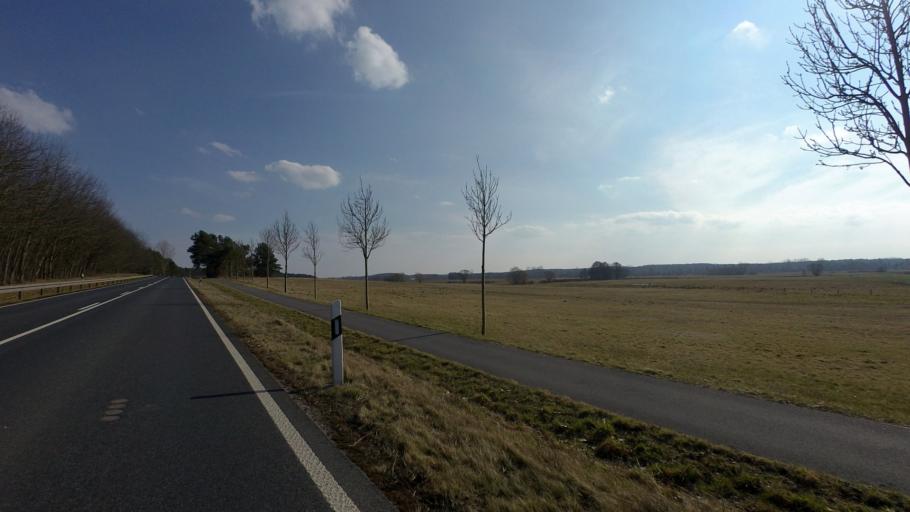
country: DE
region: Brandenburg
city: Beelitz
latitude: 52.2305
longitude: 13.0316
